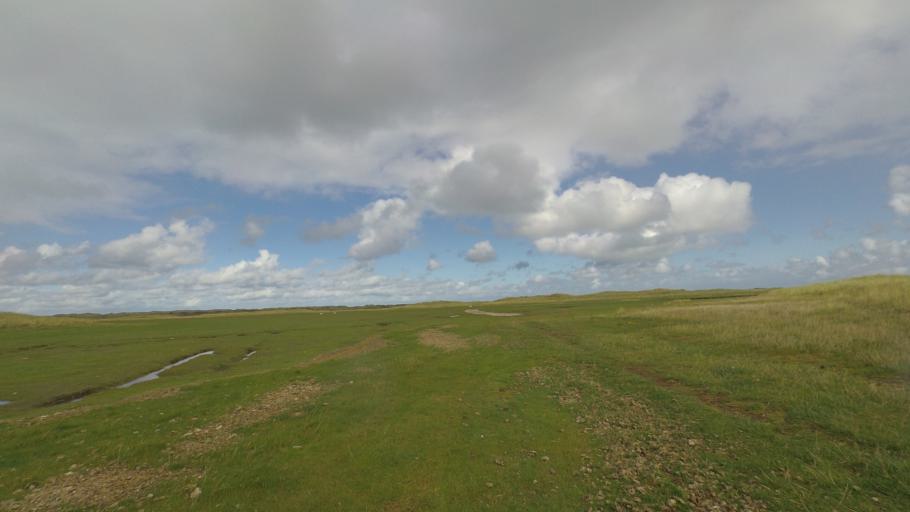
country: NL
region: Friesland
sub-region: Gemeente Ameland
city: Nes
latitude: 53.4537
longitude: 5.8623
